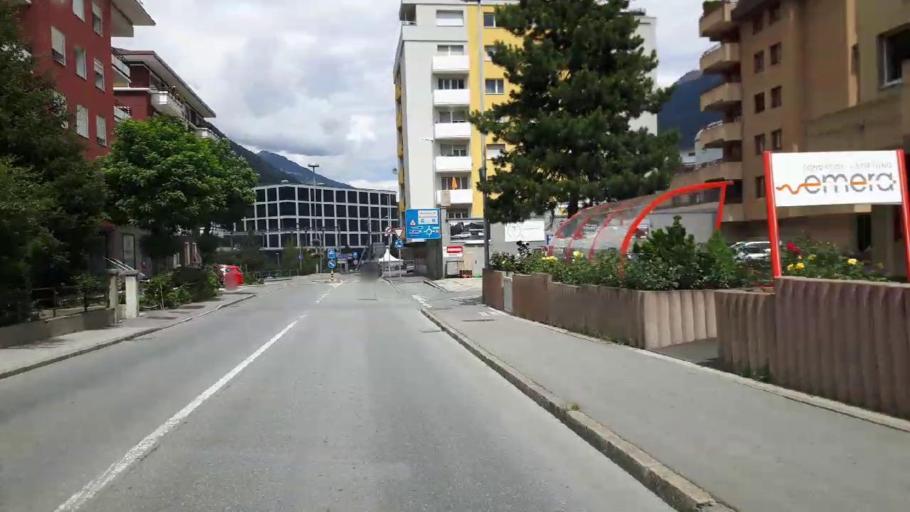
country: CH
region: Valais
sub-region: Brig District
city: Brig
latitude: 46.3180
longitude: 7.9845
